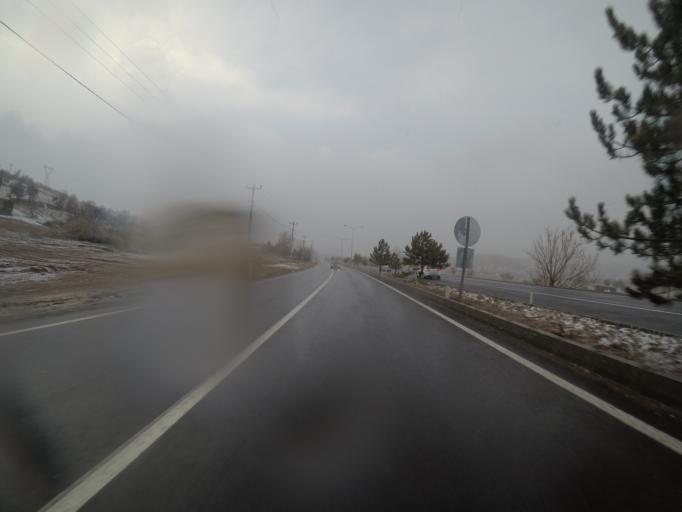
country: TR
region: Nevsehir
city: Nevsehir
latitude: 38.6309
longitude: 34.7617
